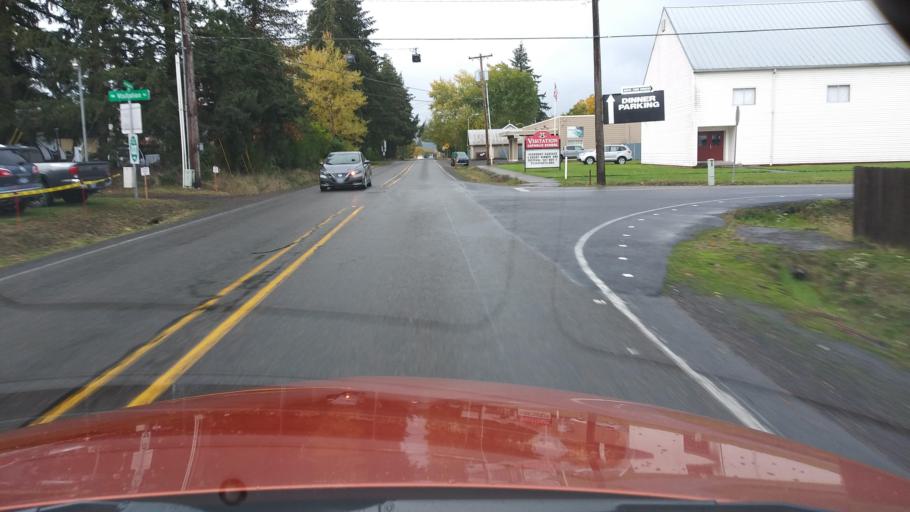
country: US
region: Oregon
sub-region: Washington County
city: Cornelius
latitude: 45.5499
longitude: -123.0842
